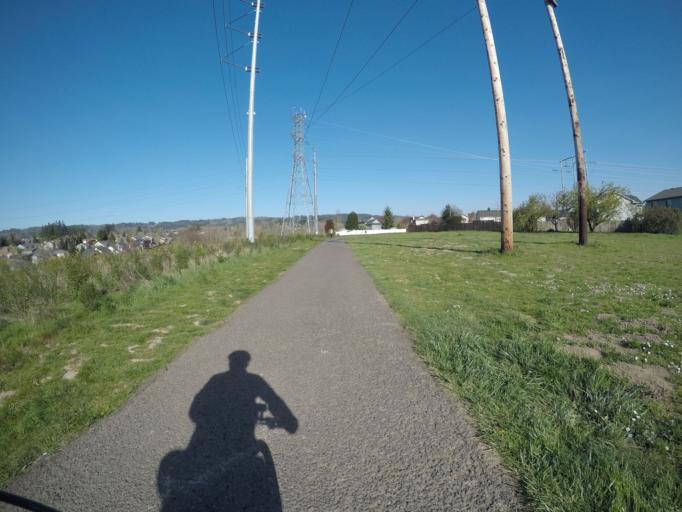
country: US
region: Oregon
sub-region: Washington County
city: Oak Hills
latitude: 45.5612
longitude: -122.8459
